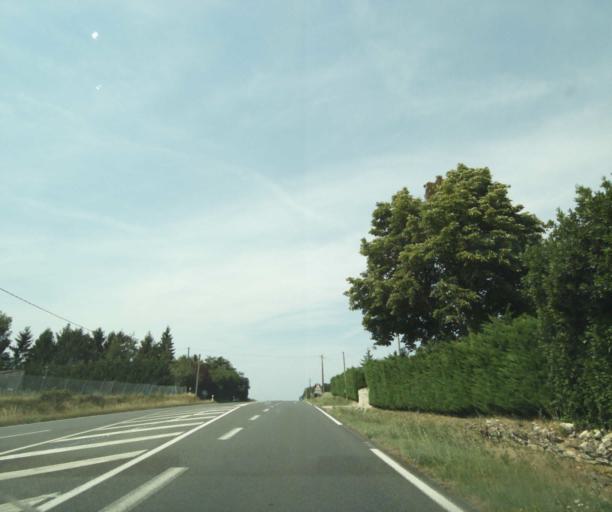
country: FR
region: Centre
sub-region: Departement d'Indre-et-Loire
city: Sainte-Maure-de-Touraine
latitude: 47.1512
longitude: 0.6465
